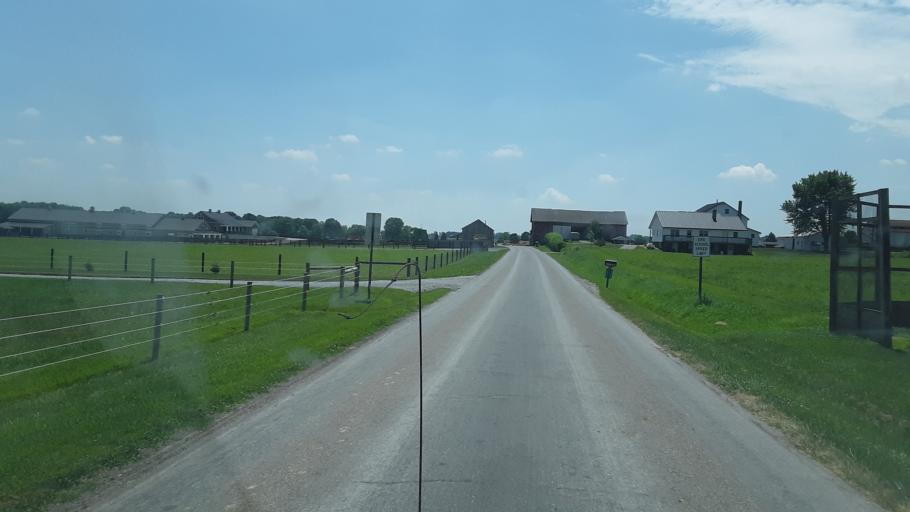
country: US
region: Ohio
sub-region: Wayne County
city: Apple Creek
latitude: 40.7107
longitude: -81.7713
